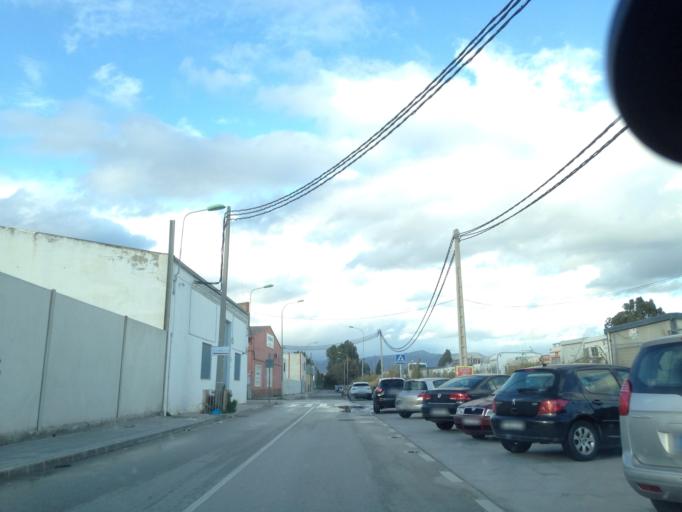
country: ES
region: Andalusia
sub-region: Provincia de Malaga
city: Torremolinos
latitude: 36.6709
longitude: -4.4699
